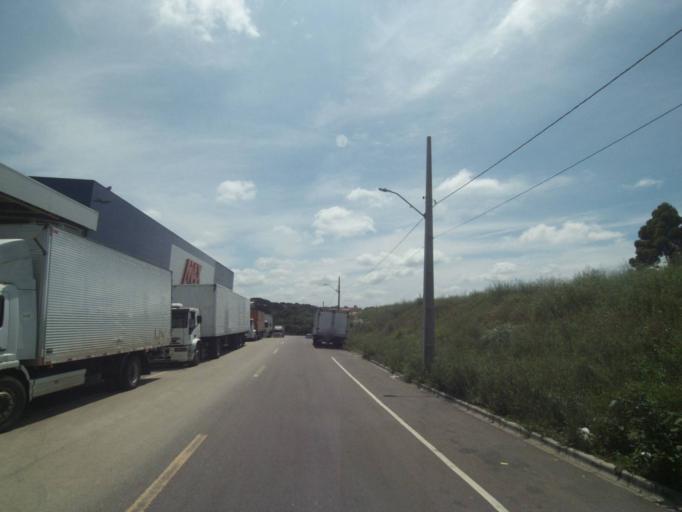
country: BR
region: Parana
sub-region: Curitiba
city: Curitiba
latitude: -25.4565
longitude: -49.3593
